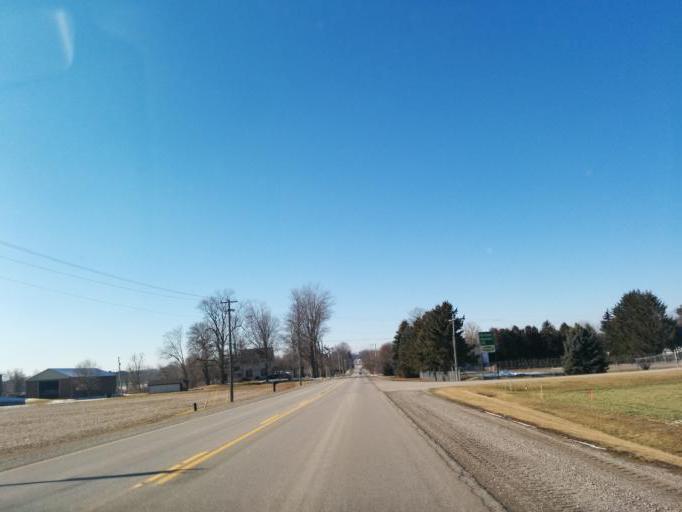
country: CA
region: Ontario
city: Brant
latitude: 43.0279
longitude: -80.3577
